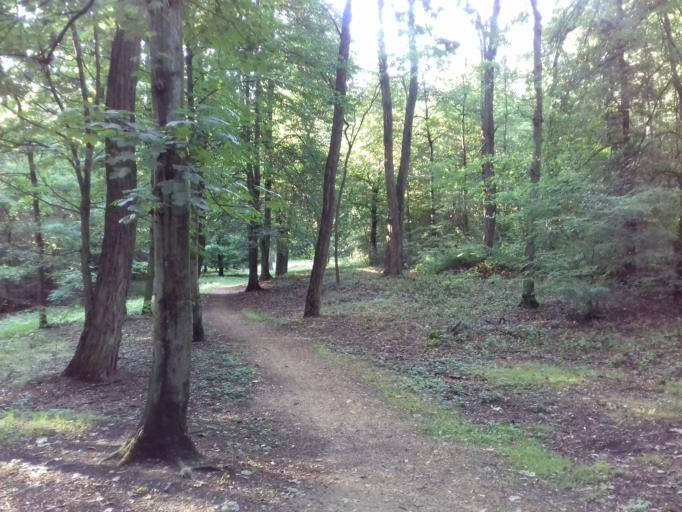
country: PL
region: Silesian Voivodeship
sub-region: Czestochowa
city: Czestochowa
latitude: 50.8393
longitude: 19.1432
